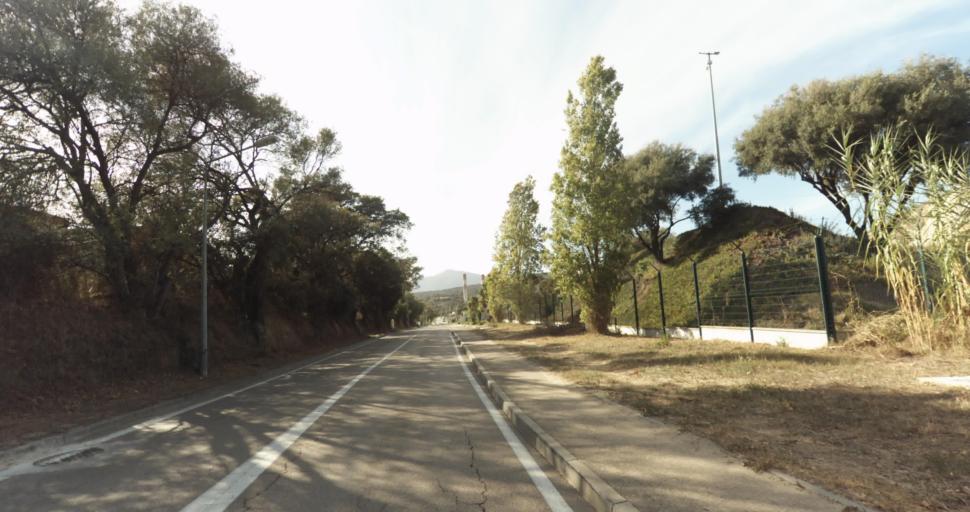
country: FR
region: Corsica
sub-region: Departement de la Corse-du-Sud
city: Afa
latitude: 41.9286
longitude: 8.7932
